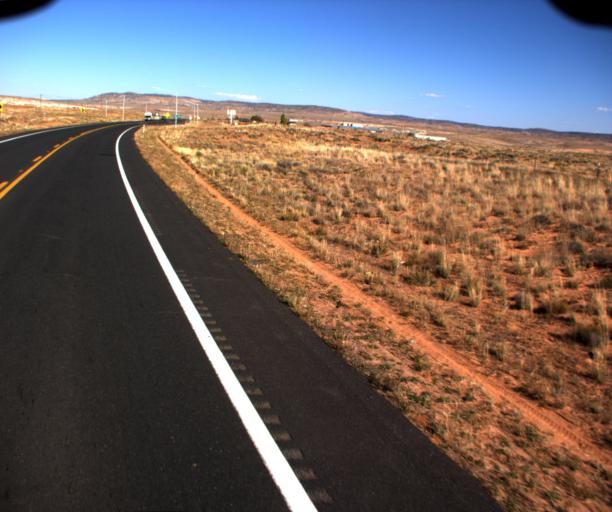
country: US
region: Arizona
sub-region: Coconino County
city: Kaibito
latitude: 36.3177
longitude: -110.9506
